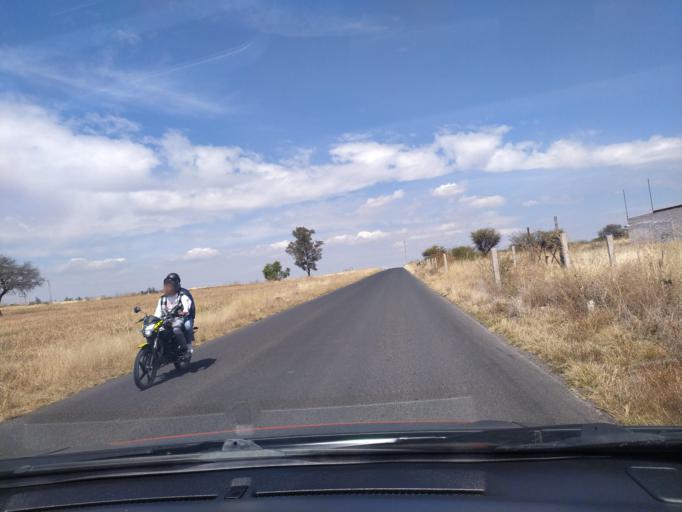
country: MX
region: Guanajuato
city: San Roque
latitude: 20.9577
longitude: -101.8302
